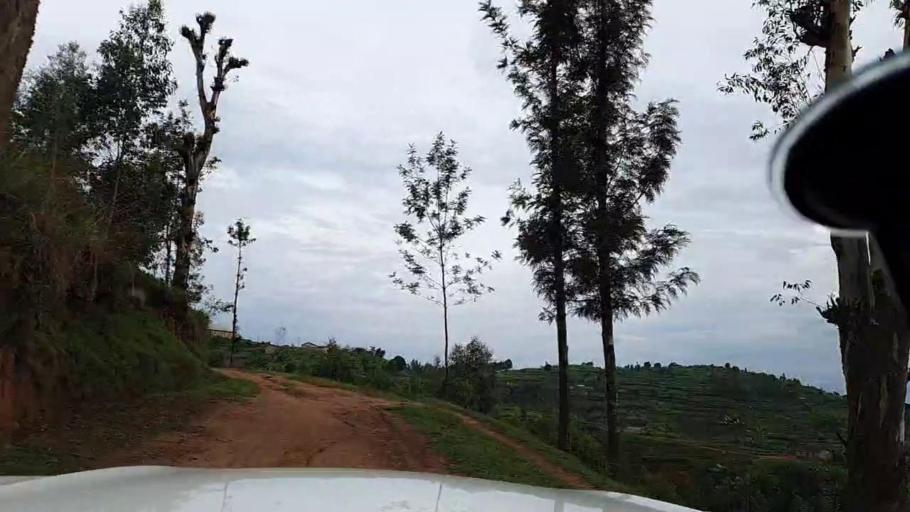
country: RW
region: Southern Province
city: Gitarama
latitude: -2.1246
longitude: 29.6515
